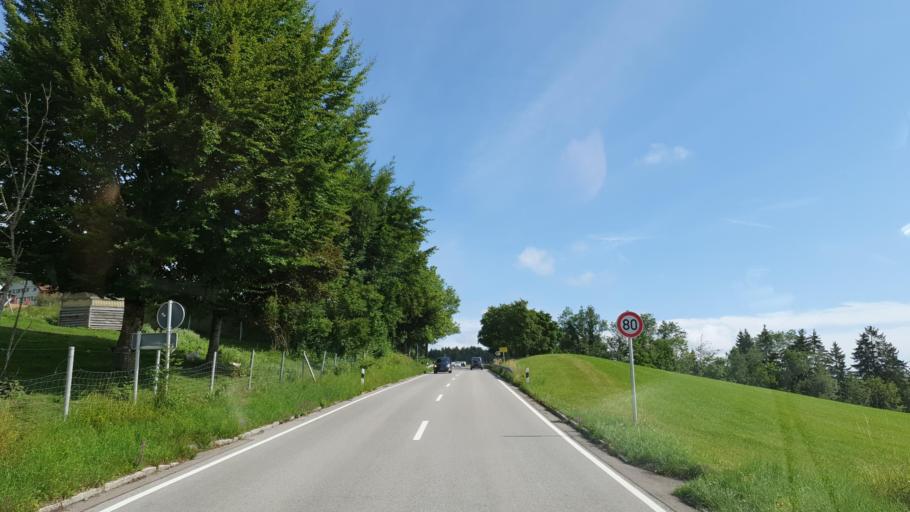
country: DE
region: Bavaria
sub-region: Swabia
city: Scheidegg
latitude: 47.5655
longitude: 9.8480
